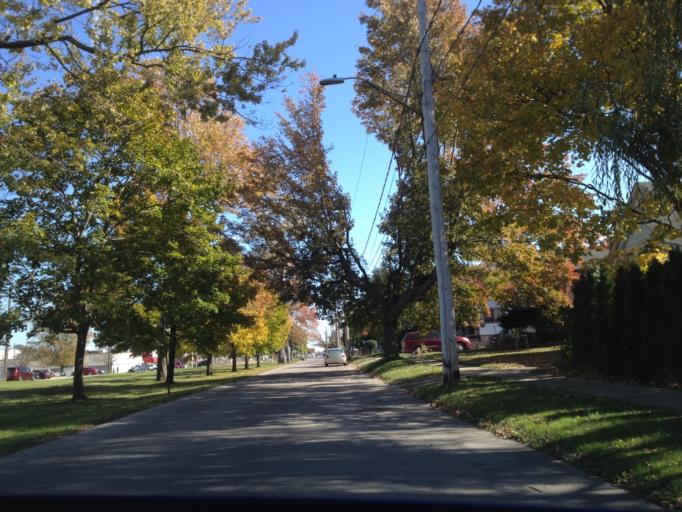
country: CA
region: Ontario
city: St. Thomas
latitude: 42.7779
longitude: -81.2060
